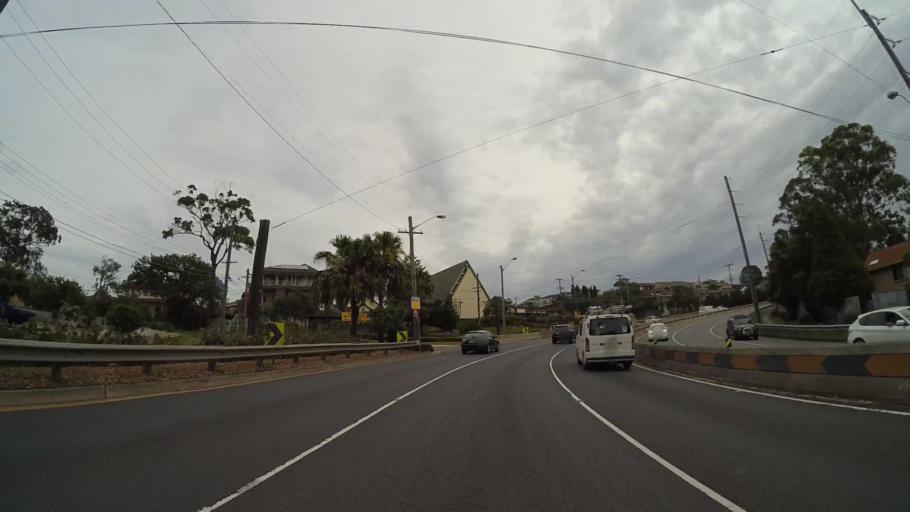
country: AU
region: New South Wales
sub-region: Kogarah
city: Blakehurst
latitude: -34.0089
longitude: 151.1106
